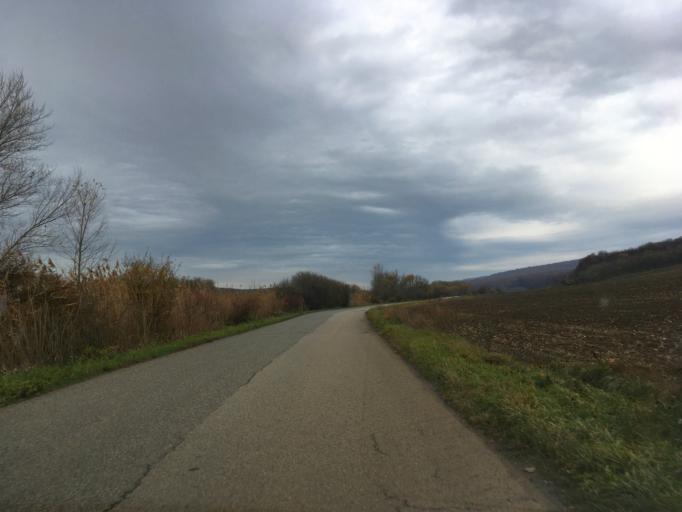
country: SK
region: Nitriansky
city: Surany
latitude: 48.0479
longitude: 18.3690
